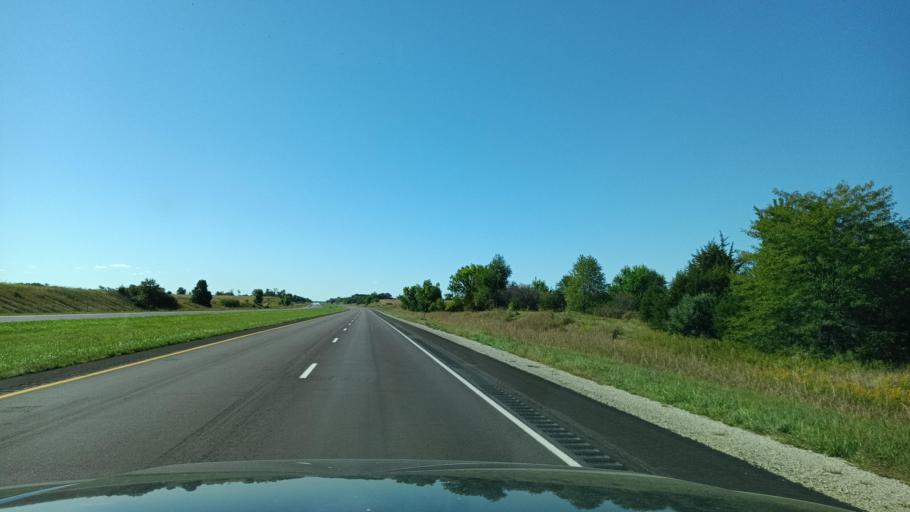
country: US
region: Illinois
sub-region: Hancock County
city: Nauvoo
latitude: 40.4980
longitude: -91.4436
